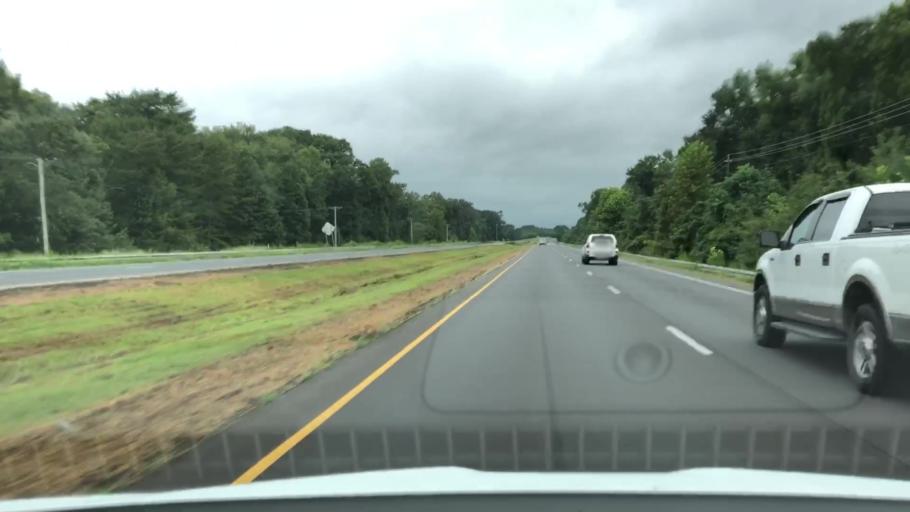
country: US
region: North Carolina
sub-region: Lenoir County
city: Kinston
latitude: 35.2617
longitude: -77.6202
